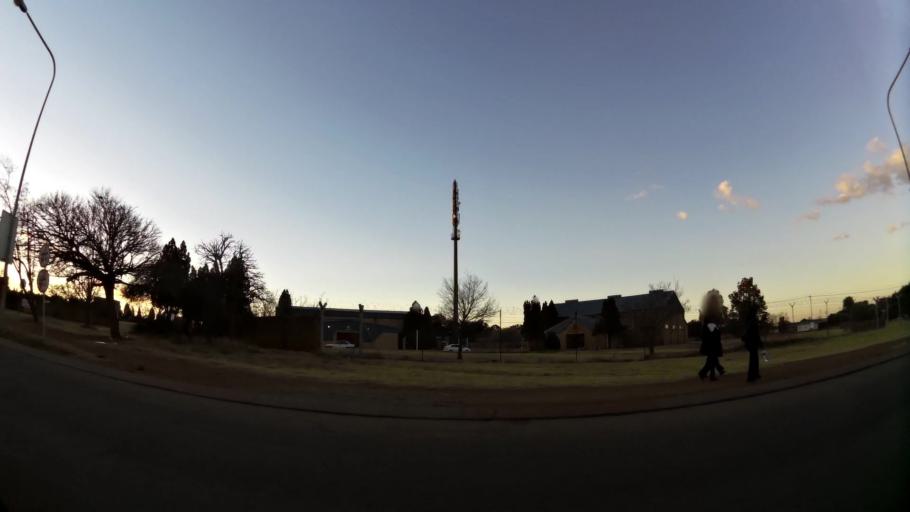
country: ZA
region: North-West
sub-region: Dr Kenneth Kaunda District Municipality
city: Potchefstroom
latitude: -26.6889
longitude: 27.0816
